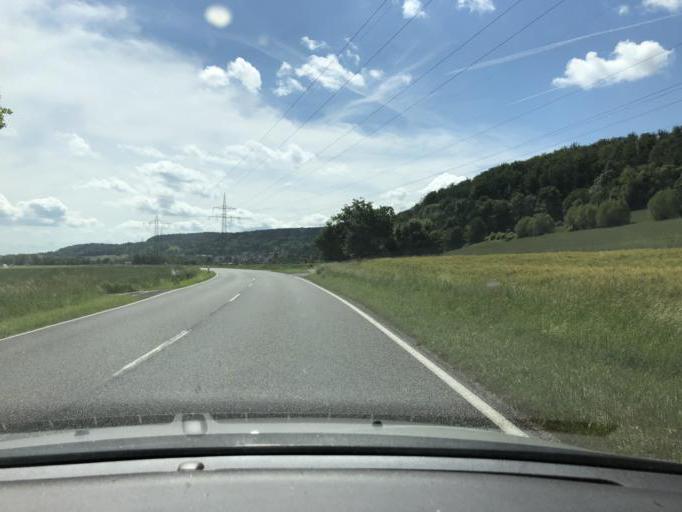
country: DE
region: Hesse
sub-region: Regierungsbezirk Kassel
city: Alheim
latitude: 51.0132
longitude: 9.6781
